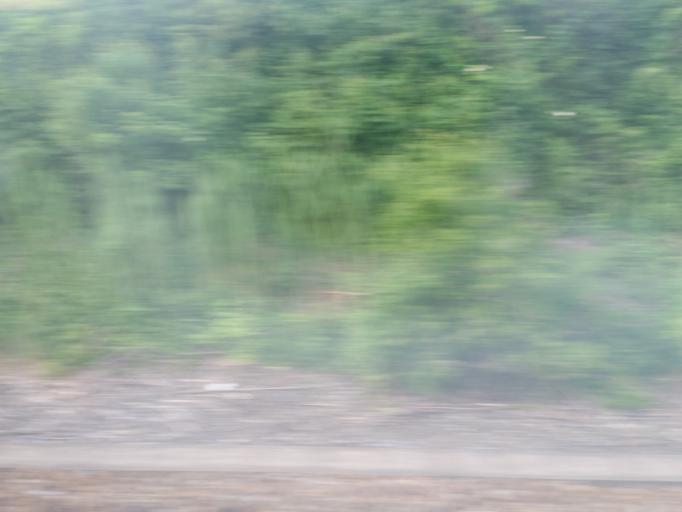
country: AT
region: Lower Austria
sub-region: Politischer Bezirk Ganserndorf
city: Marchegg
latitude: 48.2533
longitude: 16.9097
